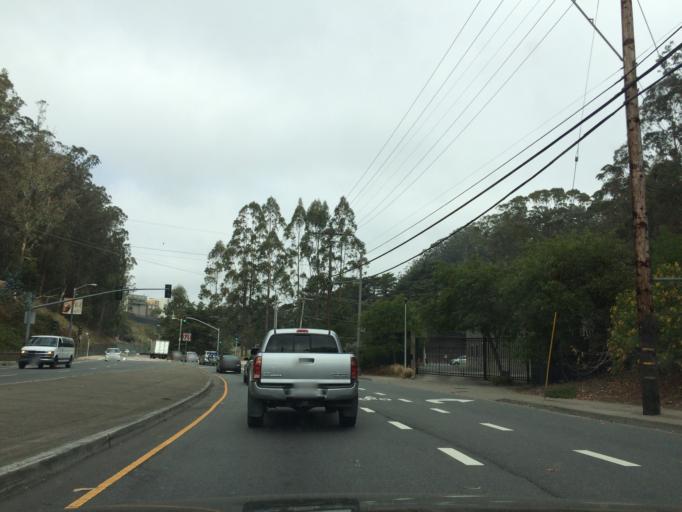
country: US
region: California
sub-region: San Mateo County
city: Daly City
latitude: 37.7508
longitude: -122.4609
